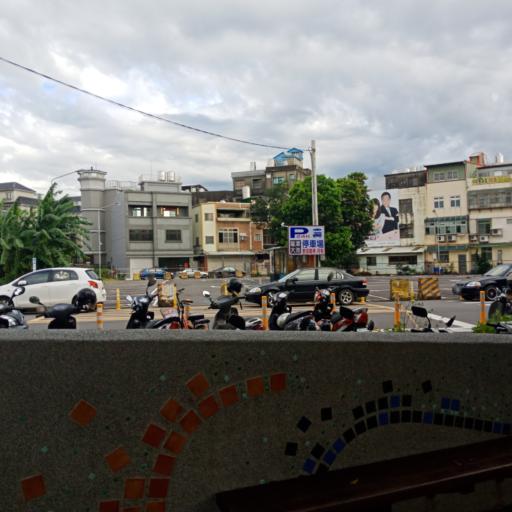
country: TW
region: Taiwan
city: Daxi
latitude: 24.8614
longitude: 121.2115
